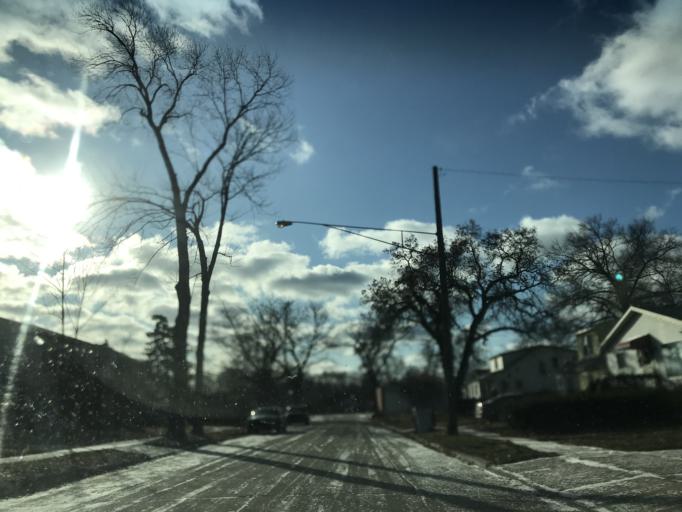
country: US
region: Michigan
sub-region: Oakland County
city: Hazel Park
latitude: 42.4627
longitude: -83.1082
